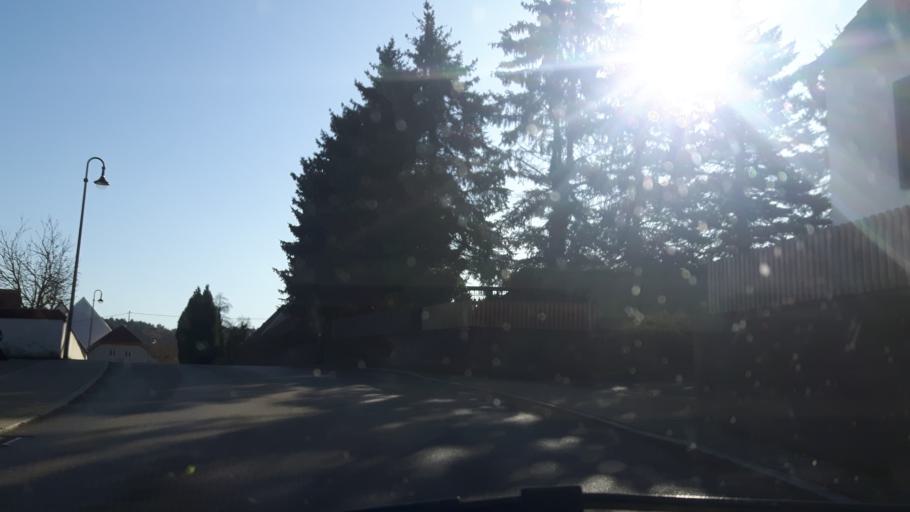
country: DE
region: Bavaria
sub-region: Swabia
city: Marxheim
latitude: 48.7791
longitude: 10.9543
